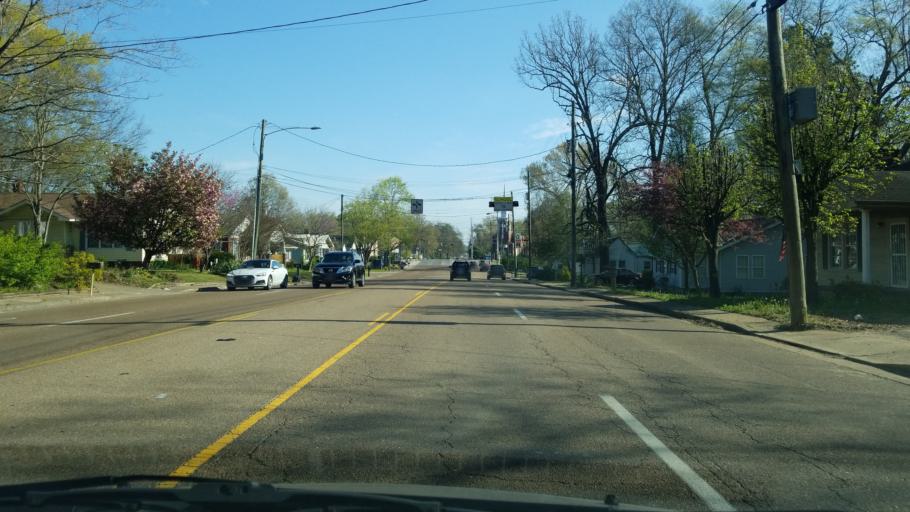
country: US
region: Tennessee
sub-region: Hamilton County
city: East Ridge
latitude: 35.0108
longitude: -85.2294
